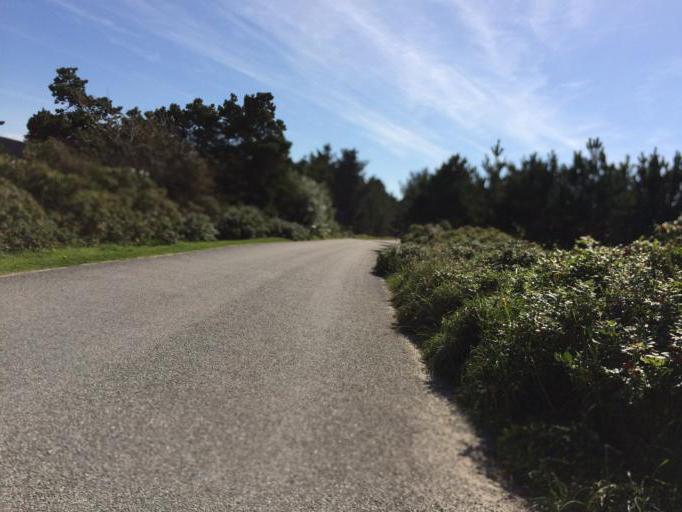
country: DK
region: Central Jutland
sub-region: Ringkobing-Skjern Kommune
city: Hvide Sande
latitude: 55.8615
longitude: 8.1749
